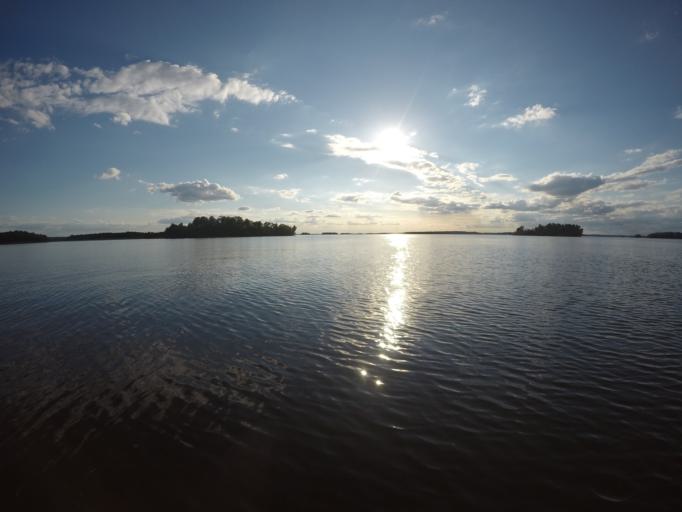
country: SE
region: Soedermanland
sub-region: Eskilstuna Kommun
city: Kvicksund
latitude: 59.4514
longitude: 16.2980
